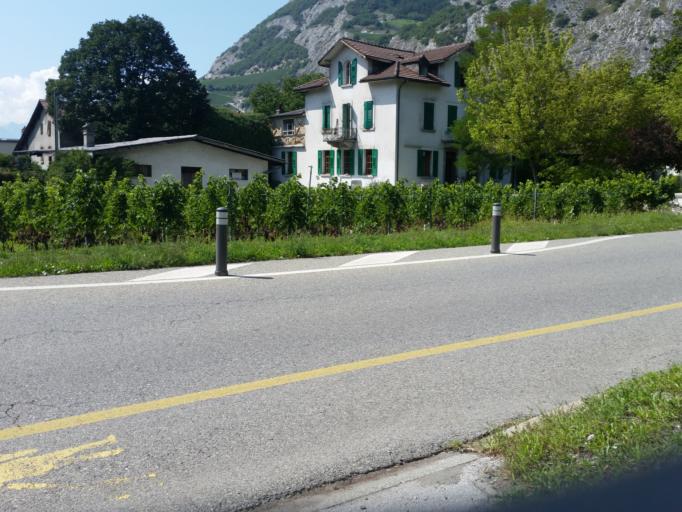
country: CH
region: Valais
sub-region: Conthey District
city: Ardon
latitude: 46.2139
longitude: 7.2627
